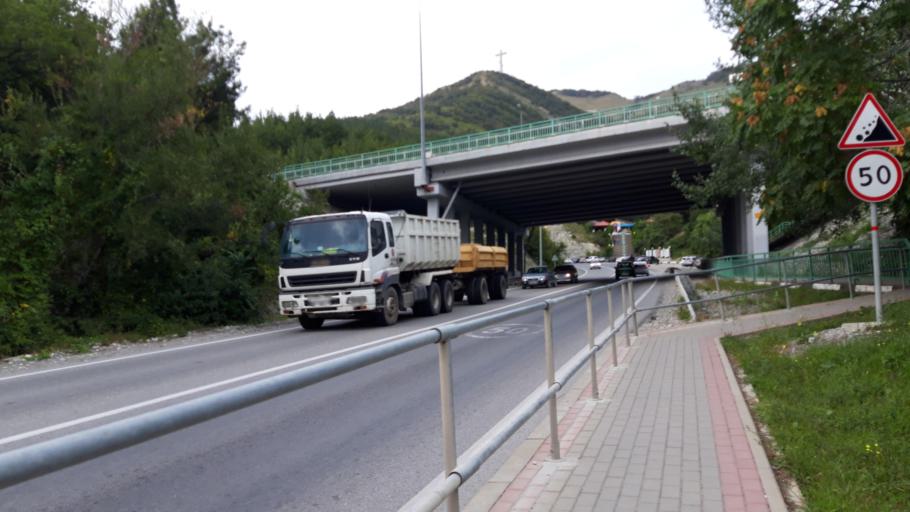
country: RU
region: Krasnodarskiy
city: Gelendzhik
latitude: 44.5753
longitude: 38.0920
